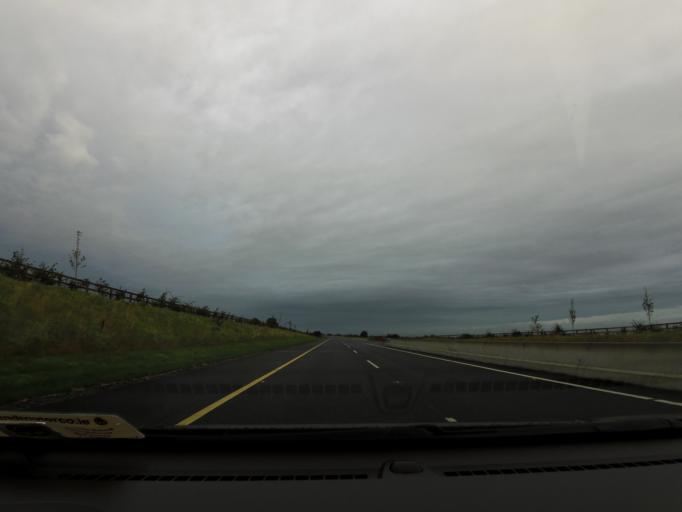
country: IE
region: Connaught
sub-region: County Galway
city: Tuam
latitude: 53.4816
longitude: -8.8634
